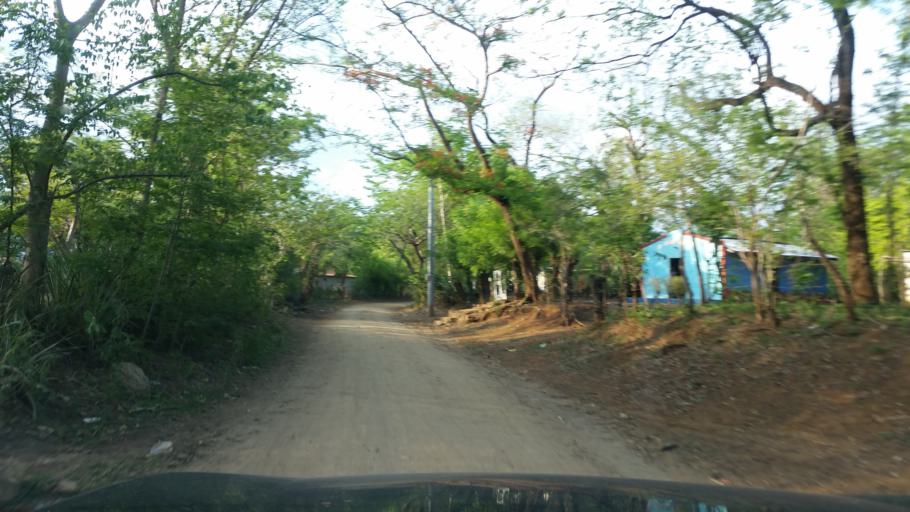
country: NI
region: Managua
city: Masachapa
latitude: 11.7967
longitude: -86.4697
